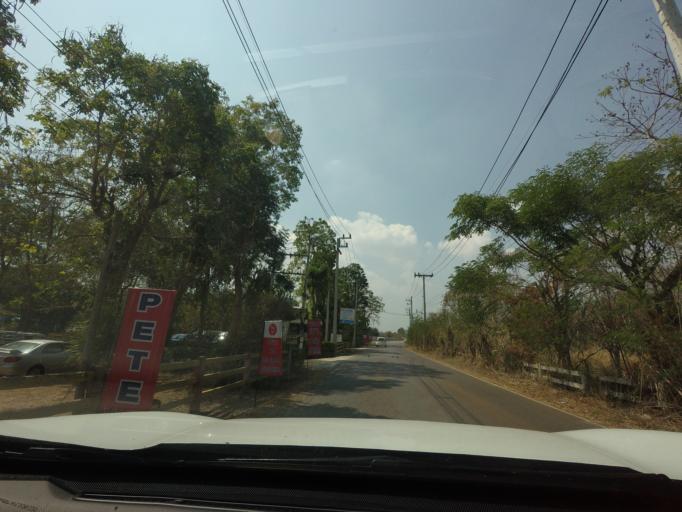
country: TH
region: Nakhon Ratchasima
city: Pak Chong
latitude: 14.5793
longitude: 101.4318
